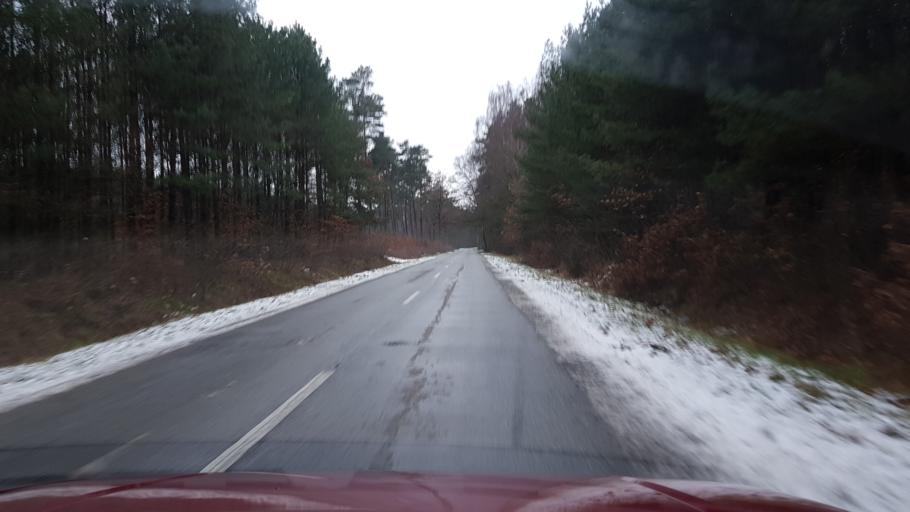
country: PL
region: West Pomeranian Voivodeship
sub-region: Powiat gryficki
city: Ploty
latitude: 53.6956
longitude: 15.2657
